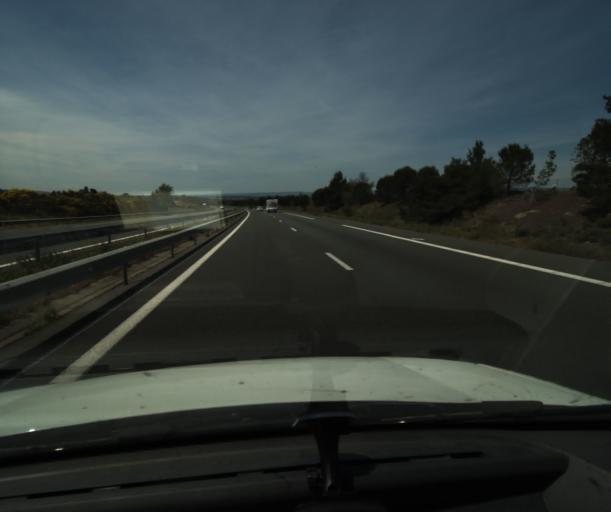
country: FR
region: Languedoc-Roussillon
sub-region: Departement de l'Aude
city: Capendu
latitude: 43.1755
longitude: 2.5984
